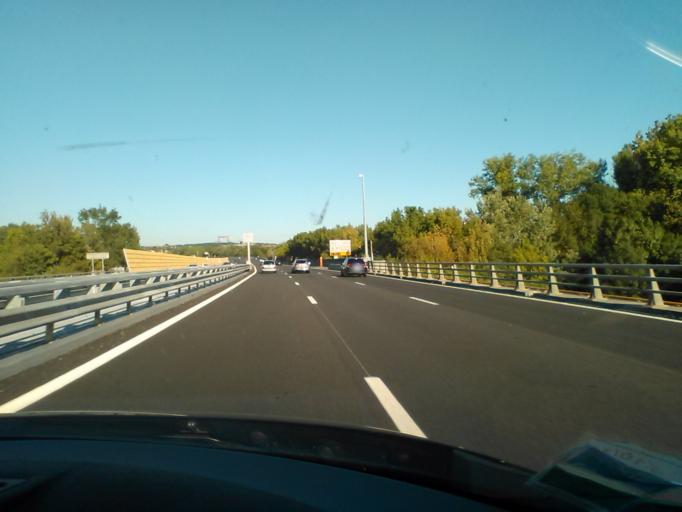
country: FR
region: Rhone-Alpes
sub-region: Departement du Rhone
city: Quincieux
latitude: 45.9038
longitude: 4.8054
